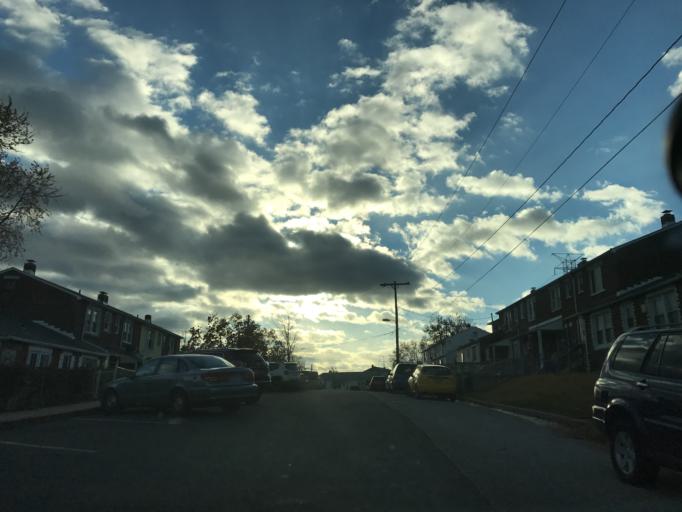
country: US
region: Maryland
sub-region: Baltimore County
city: Rosedale
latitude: 39.3103
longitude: -76.5577
